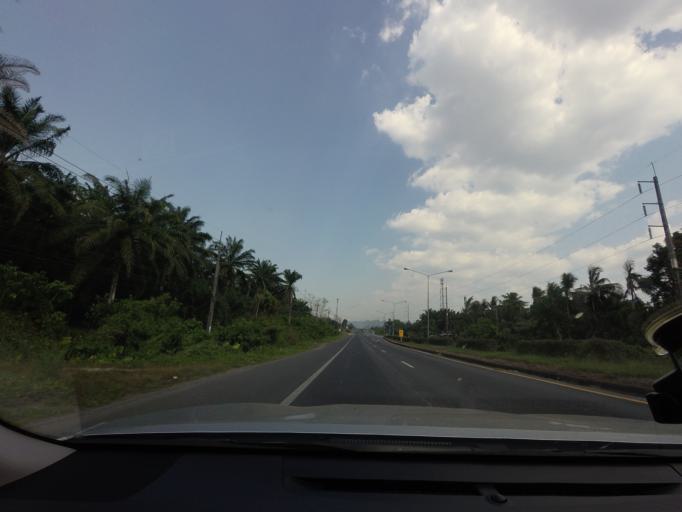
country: TH
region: Phangnga
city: Thap Put
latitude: 8.5075
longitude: 98.6744
